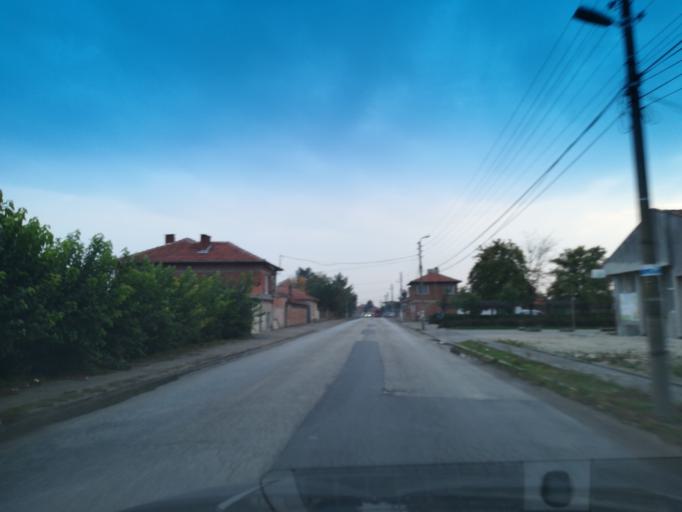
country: BG
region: Stara Zagora
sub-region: Obshtina Chirpan
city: Chirpan
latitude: 42.1755
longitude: 25.2094
